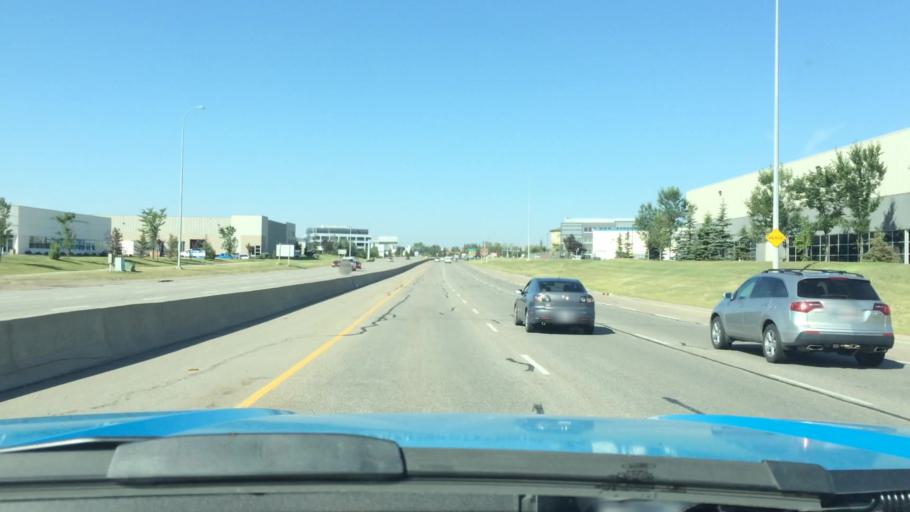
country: CA
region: Alberta
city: Calgary
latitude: 51.0948
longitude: -113.9926
